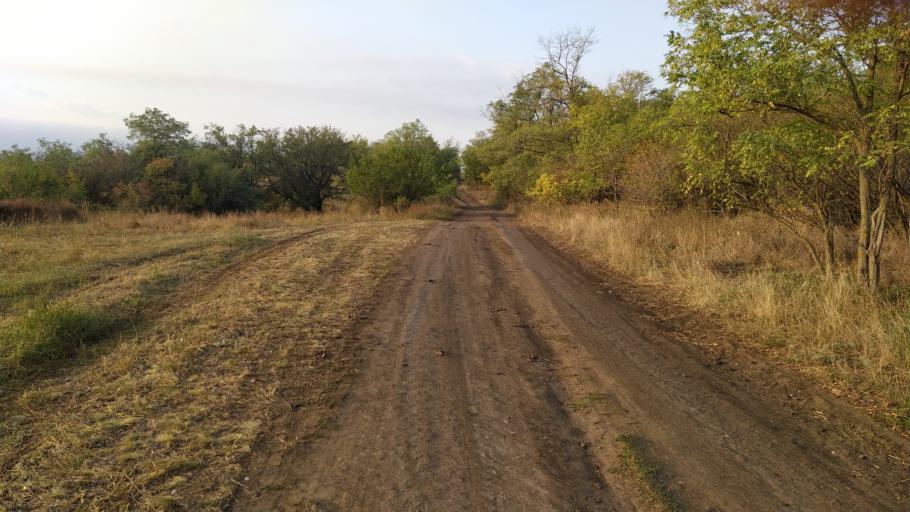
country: RU
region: Rostov
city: Gornyy
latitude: 47.8898
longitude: 40.2411
